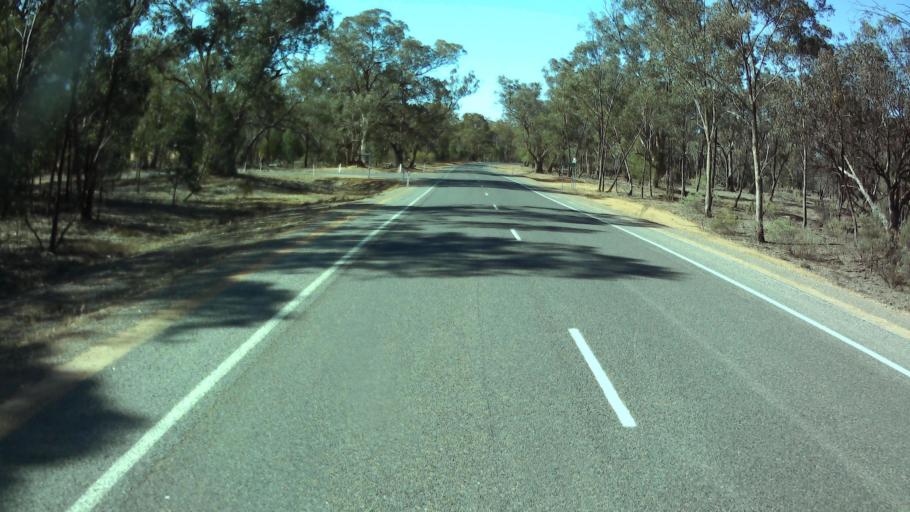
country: AU
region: New South Wales
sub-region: Weddin
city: Grenfell
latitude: -33.7579
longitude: 148.0826
